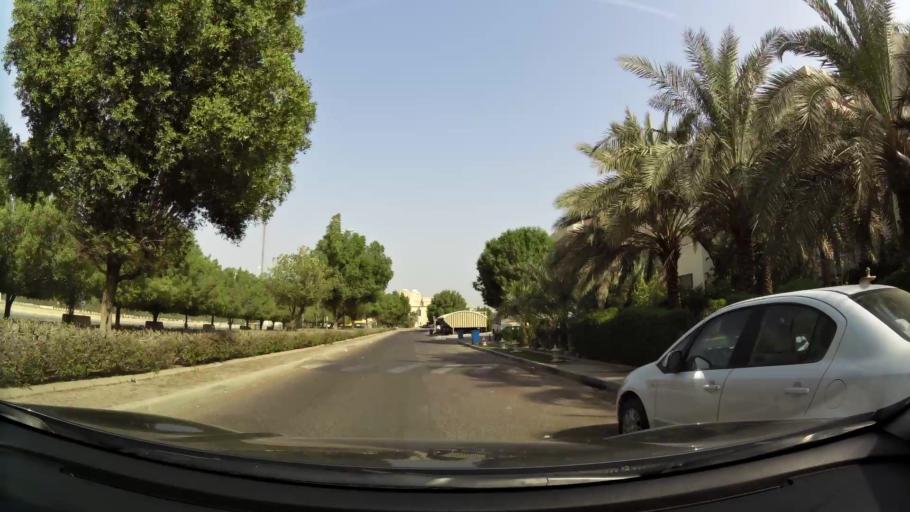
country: KW
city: Bayan
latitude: 29.2899
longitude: 48.0487
